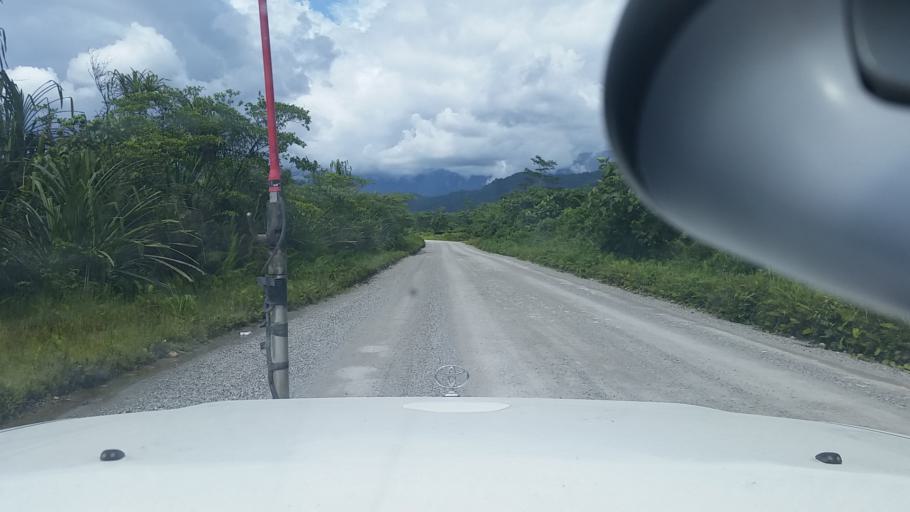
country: PG
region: Western Province
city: Kiunga
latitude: -5.3843
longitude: 141.2966
